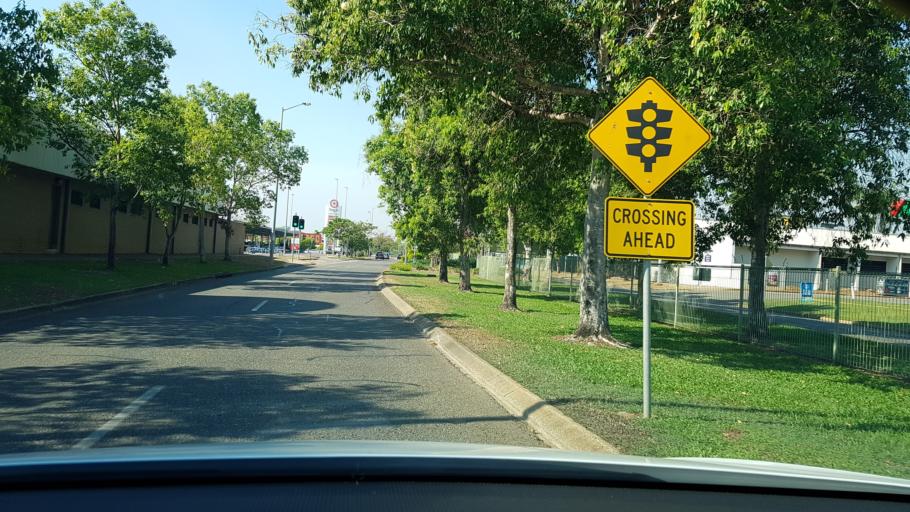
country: AU
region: Northern Territory
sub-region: Palmerston
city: Palmerston
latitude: -12.4820
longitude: 130.9854
